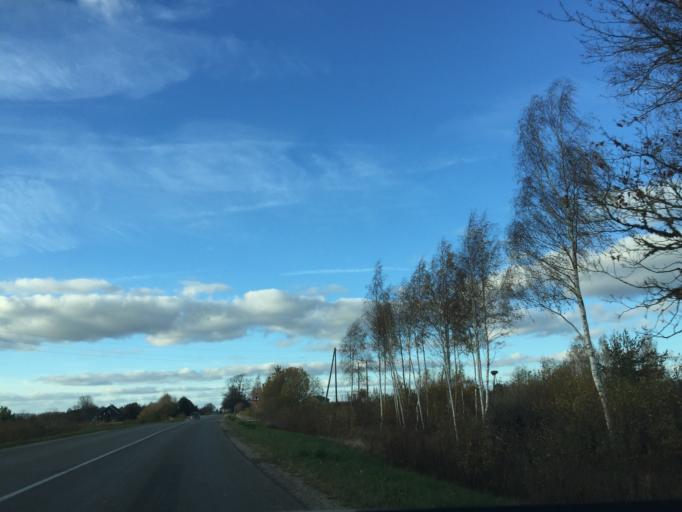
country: LV
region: Tukuma Rajons
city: Tukums
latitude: 56.9868
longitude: 23.1026
